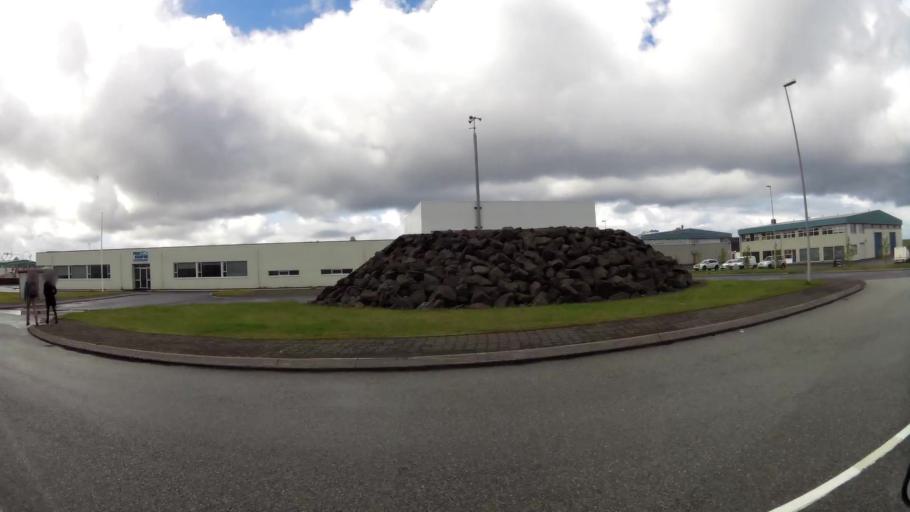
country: IS
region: Capital Region
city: Reykjavik
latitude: 64.1568
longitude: -21.9415
